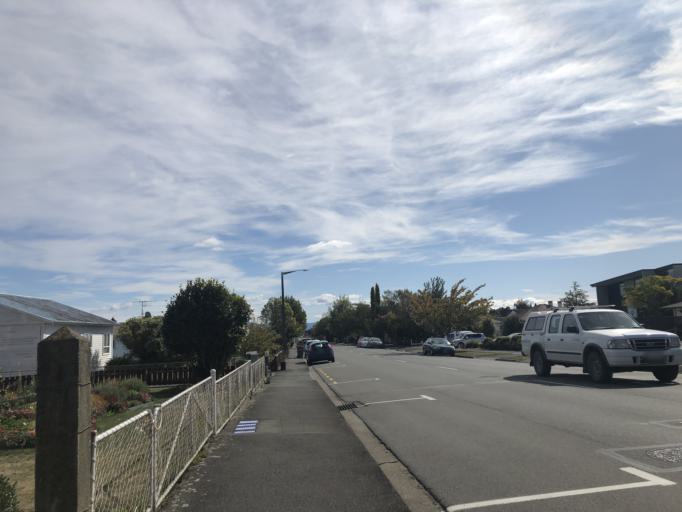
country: NZ
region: Tasman
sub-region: Tasman District
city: Richmond
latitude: -41.3412
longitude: 173.1845
